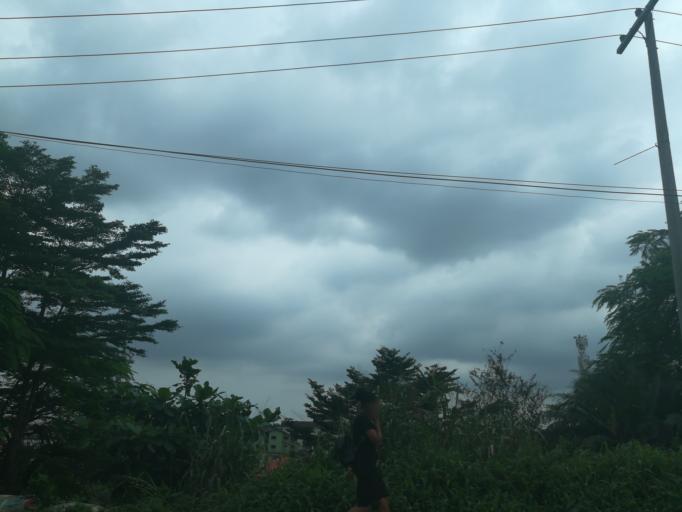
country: NG
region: Lagos
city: Ikeja
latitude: 6.6086
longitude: 3.3515
